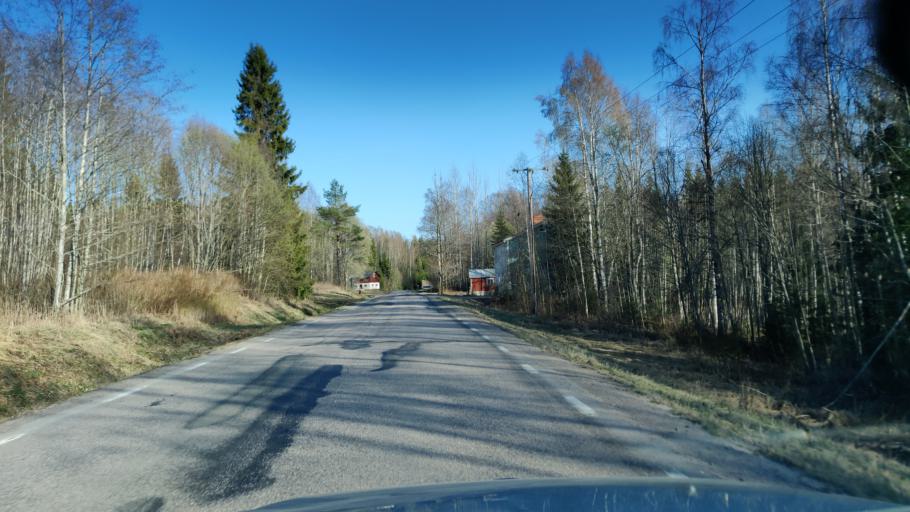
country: SE
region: Vaermland
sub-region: Munkfors Kommun
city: Munkfors
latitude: 59.9846
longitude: 13.3988
